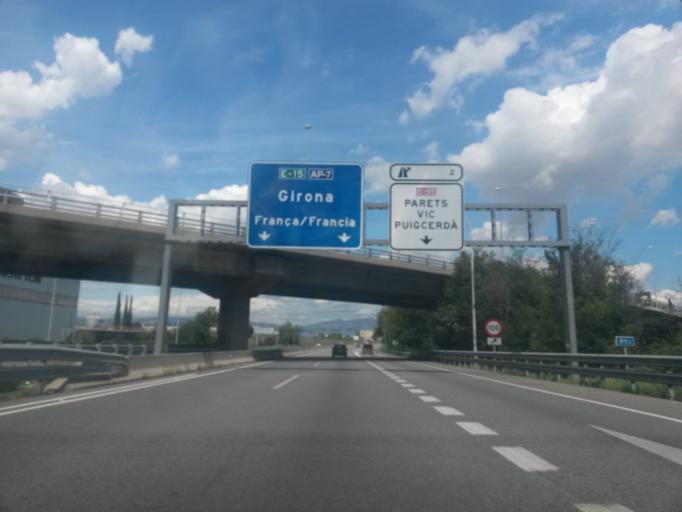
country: ES
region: Catalonia
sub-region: Provincia de Barcelona
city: Montmelo
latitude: 41.5487
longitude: 2.2355
